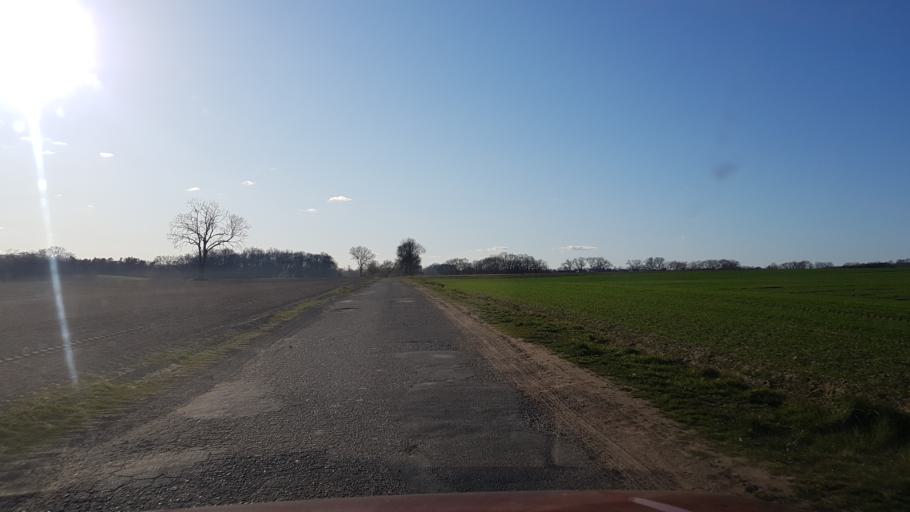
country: PL
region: West Pomeranian Voivodeship
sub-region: Powiat stargardzki
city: Stara Dabrowa
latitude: 53.3808
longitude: 15.1098
